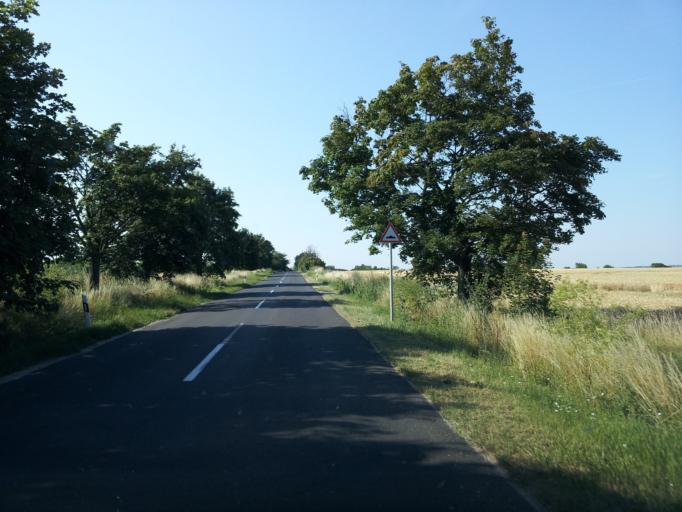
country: HU
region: Fejer
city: Lovasbereny
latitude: 47.3926
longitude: 18.5864
